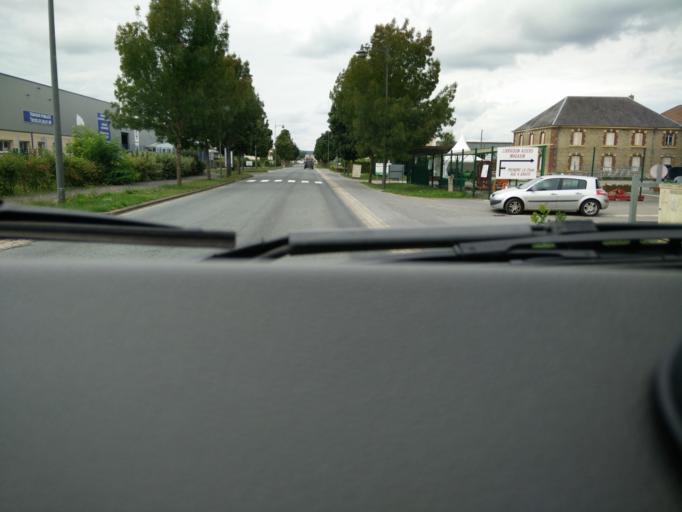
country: FR
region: Champagne-Ardenne
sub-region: Departement des Ardennes
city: Douzy
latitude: 49.6717
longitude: 5.0350
